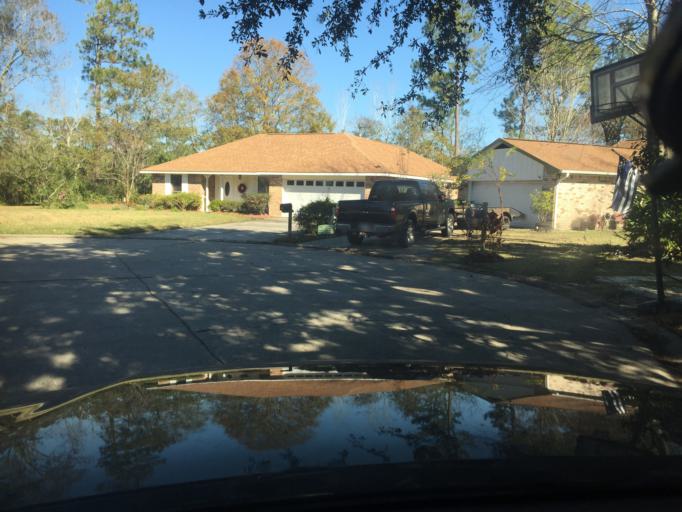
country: US
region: Louisiana
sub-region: Saint Tammany Parish
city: Slidell
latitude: 30.3009
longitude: -89.7407
